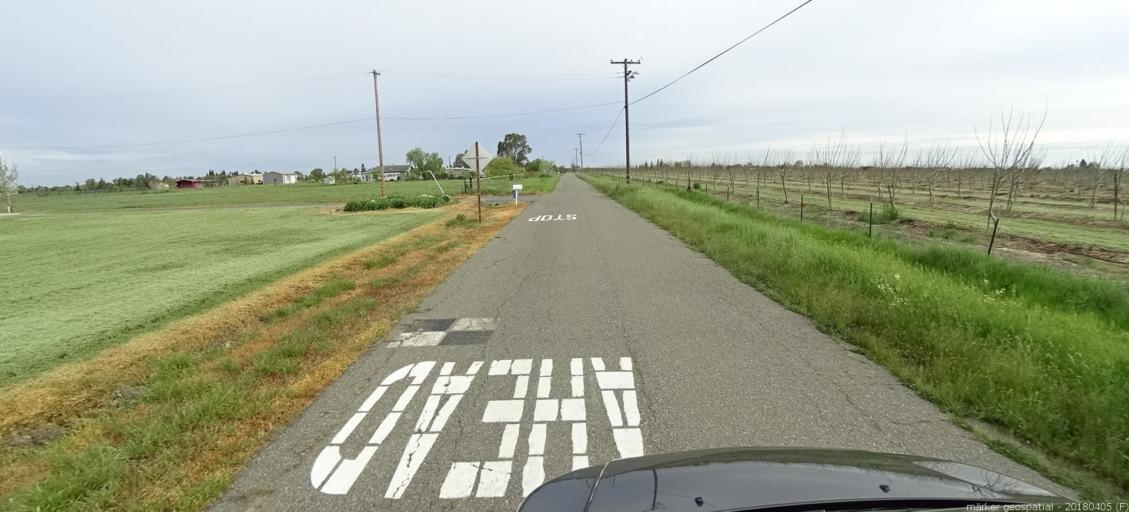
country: US
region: California
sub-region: Sacramento County
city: Herald
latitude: 38.2932
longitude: -121.2553
